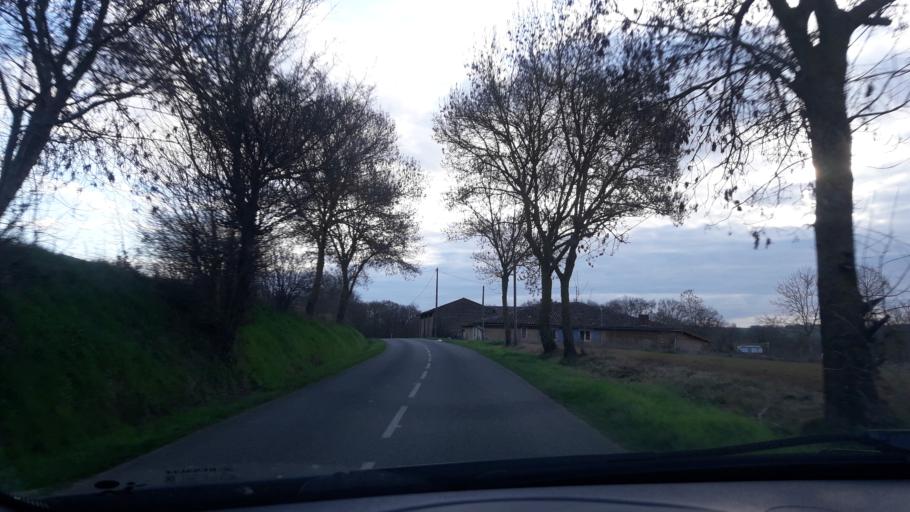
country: FR
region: Midi-Pyrenees
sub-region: Departement de la Haute-Garonne
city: Levignac
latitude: 43.6511
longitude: 1.1397
